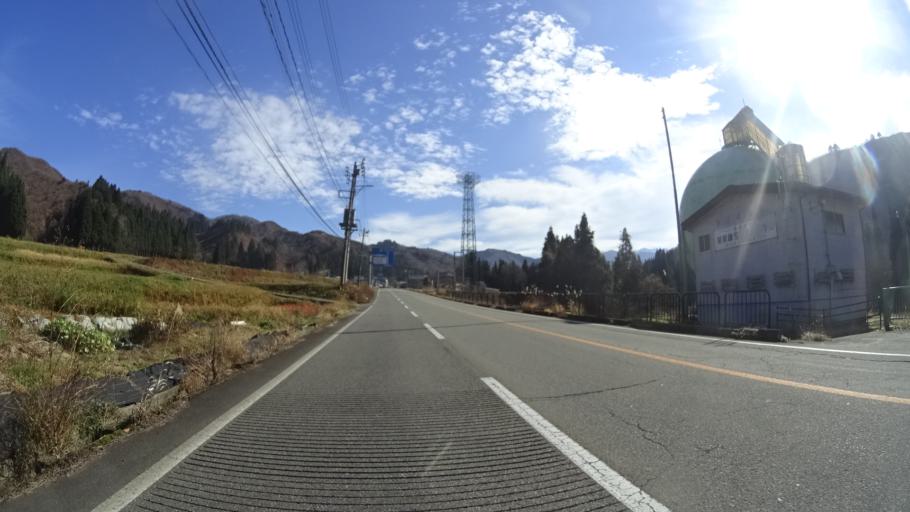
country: JP
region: Niigata
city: Muikamachi
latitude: 37.2059
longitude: 139.0682
